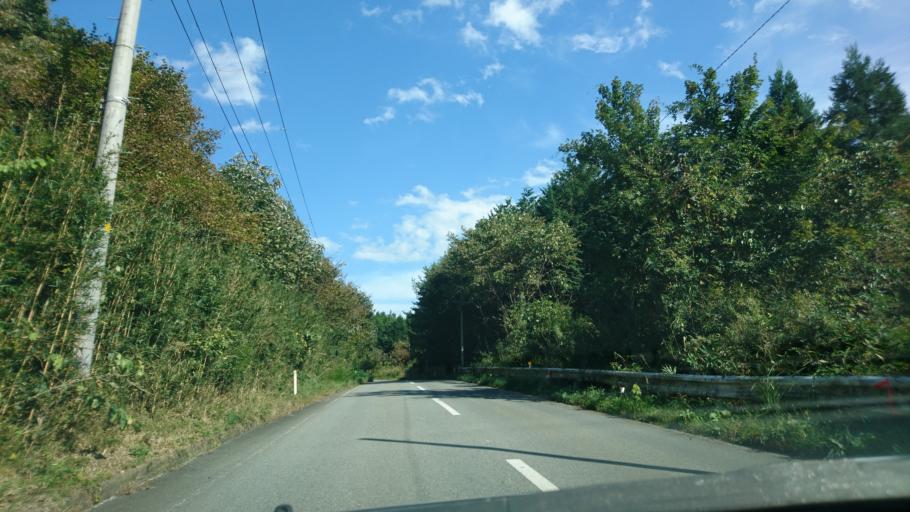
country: JP
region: Iwate
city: Ichinoseki
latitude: 38.8513
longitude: 141.0425
